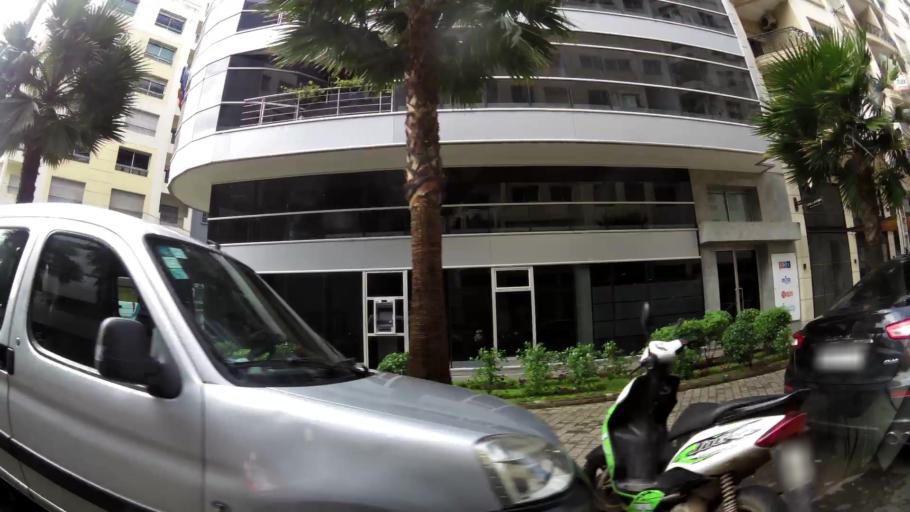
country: MA
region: Grand Casablanca
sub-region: Casablanca
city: Casablanca
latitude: 33.5823
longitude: -7.6253
